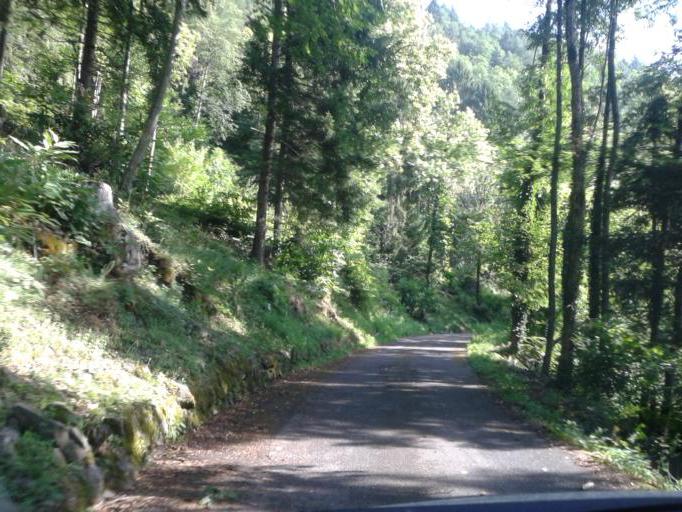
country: IT
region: Trentino-Alto Adige
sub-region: Provincia di Trento
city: Storo
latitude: 45.8606
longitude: 10.5567
